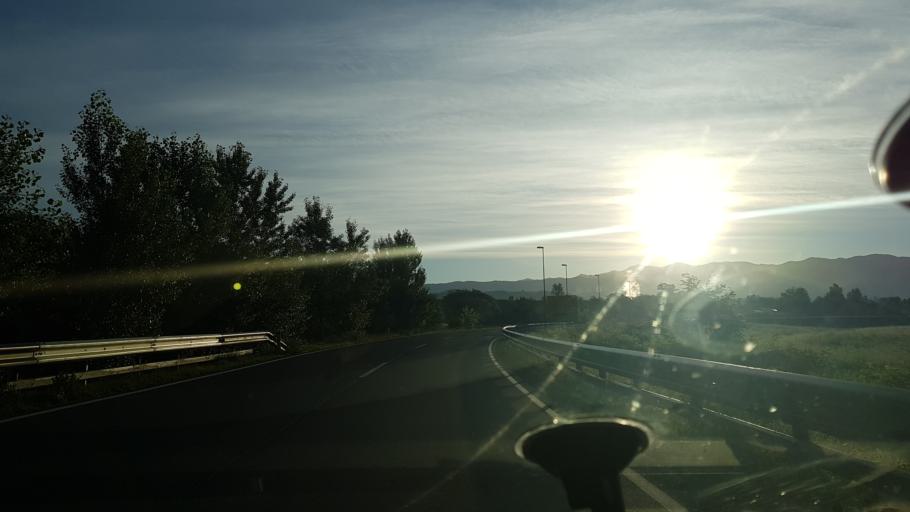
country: SI
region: Miren-Kostanjevica
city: Miren
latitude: 45.9058
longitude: 13.6196
